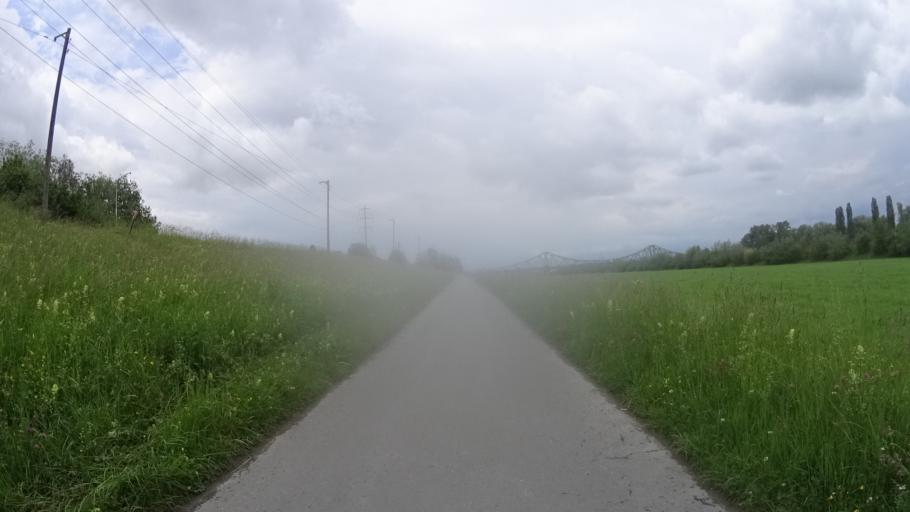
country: CH
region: Saint Gallen
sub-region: Wahlkreis Rheintal
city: Diepoldsau
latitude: 47.4049
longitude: 9.6499
